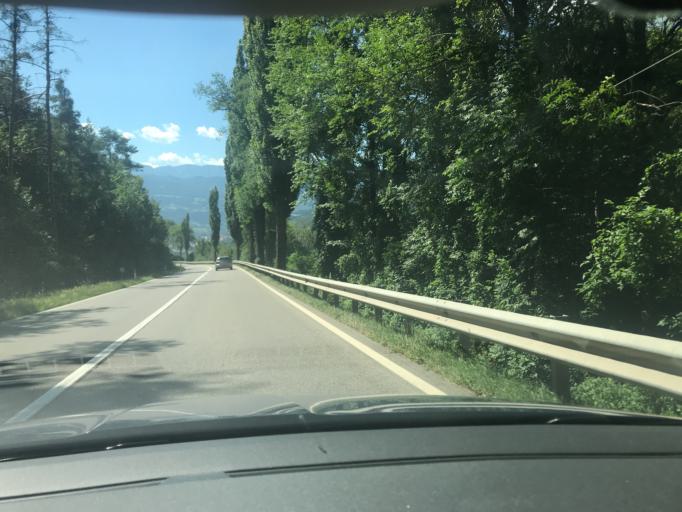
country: IT
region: Trentino-Alto Adige
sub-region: Bolzano
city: Varna
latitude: 46.7500
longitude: 11.6471
